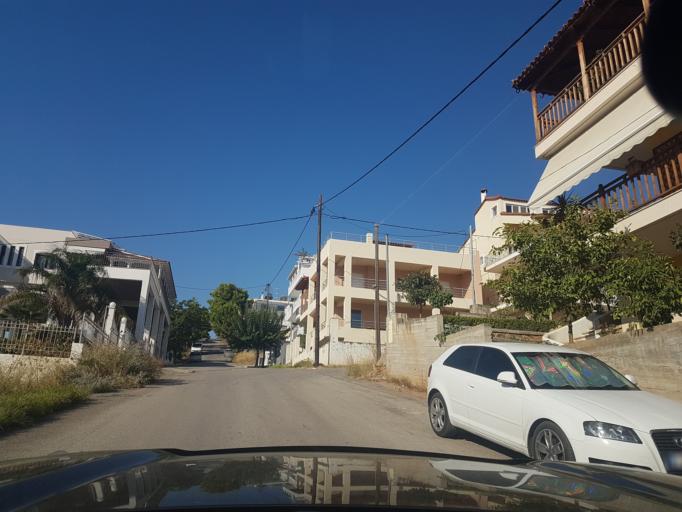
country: GR
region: Central Greece
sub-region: Nomos Evvoias
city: Chalkida
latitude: 38.4753
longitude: 23.5871
